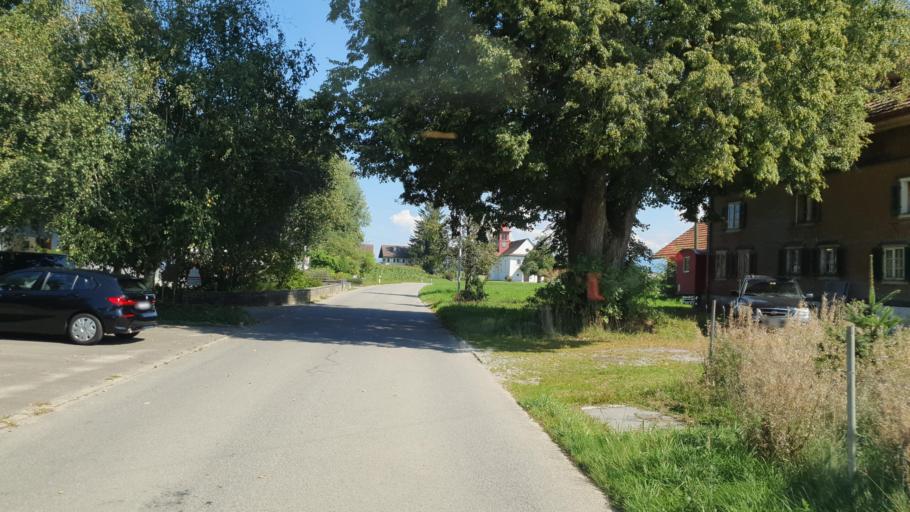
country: CH
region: Lucerne
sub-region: Hochdorf District
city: Inwil
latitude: 47.1487
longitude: 8.3513
